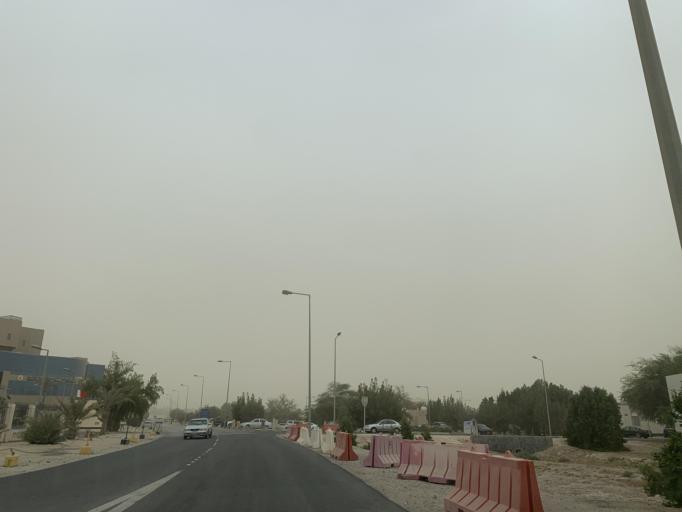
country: BH
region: Central Governorate
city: Madinat Hamad
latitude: 26.1365
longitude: 50.5212
